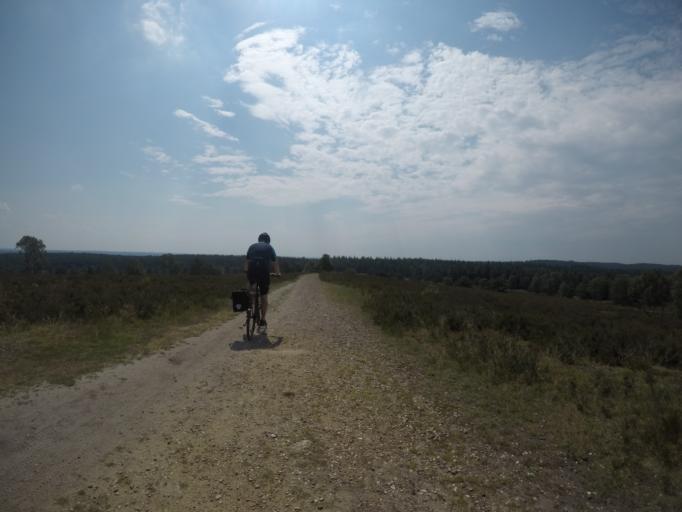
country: DE
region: Lower Saxony
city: Buchholz in der Nordheide
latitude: 53.2995
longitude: 9.8323
